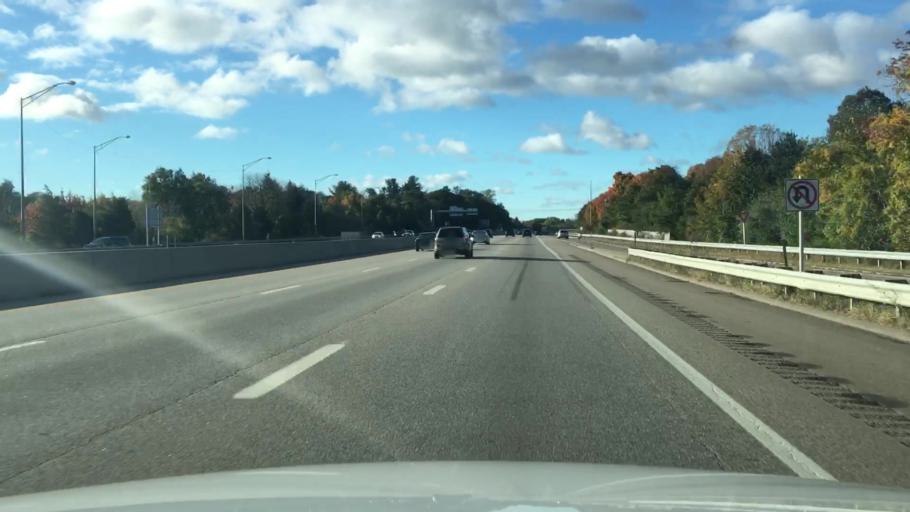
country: US
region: New Hampshire
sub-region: Rockingham County
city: Portsmouth
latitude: 43.0827
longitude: -70.7745
